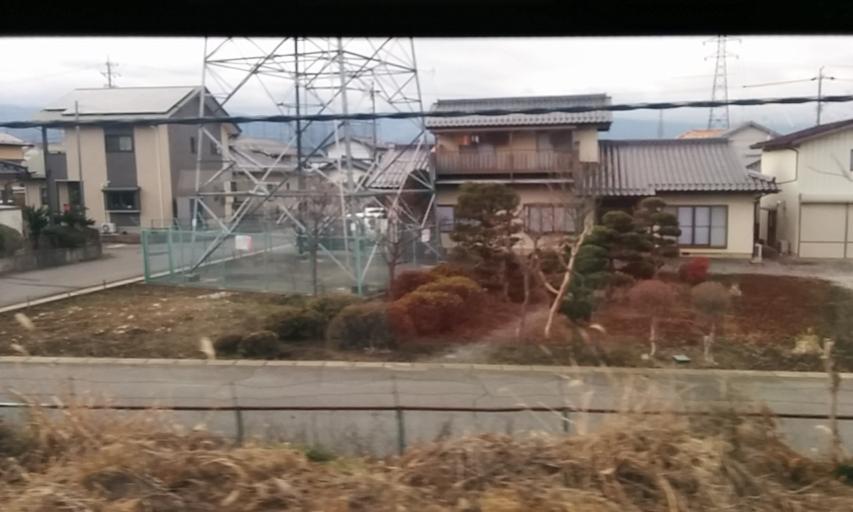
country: JP
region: Nagano
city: Shiojiri
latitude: 36.1219
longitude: 137.9481
